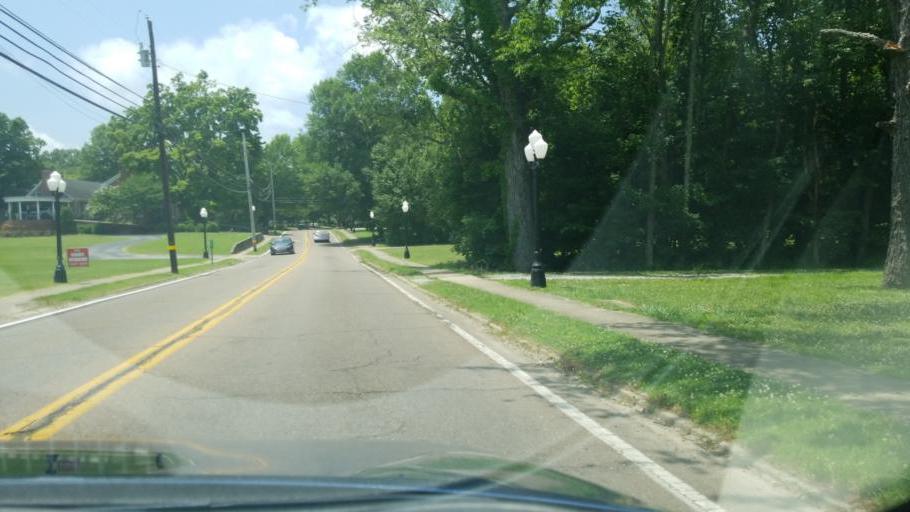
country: US
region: Tennessee
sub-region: Carroll County
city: Huntingdon
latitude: 36.0026
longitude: -88.4219
